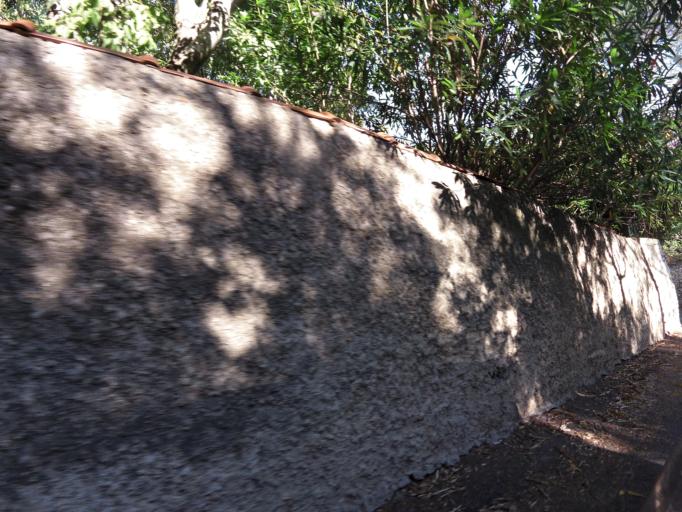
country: FR
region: Languedoc-Roussillon
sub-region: Departement du Gard
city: Nimes
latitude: 43.8579
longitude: 4.3738
